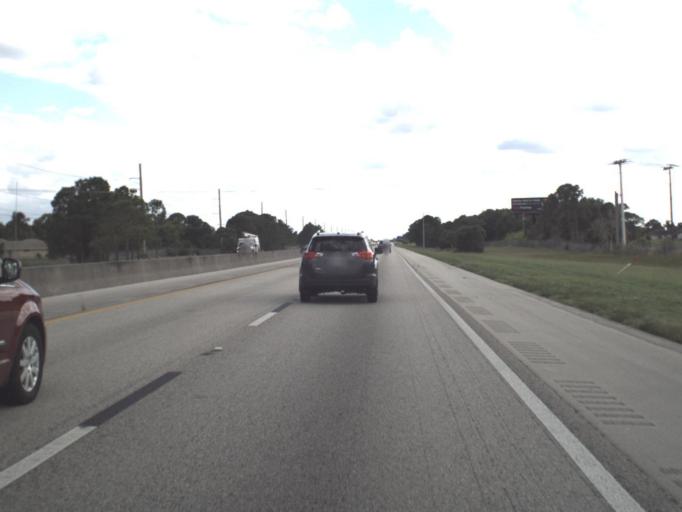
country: US
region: Florida
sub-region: Saint Lucie County
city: Port Saint Lucie
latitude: 27.2509
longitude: -80.3480
